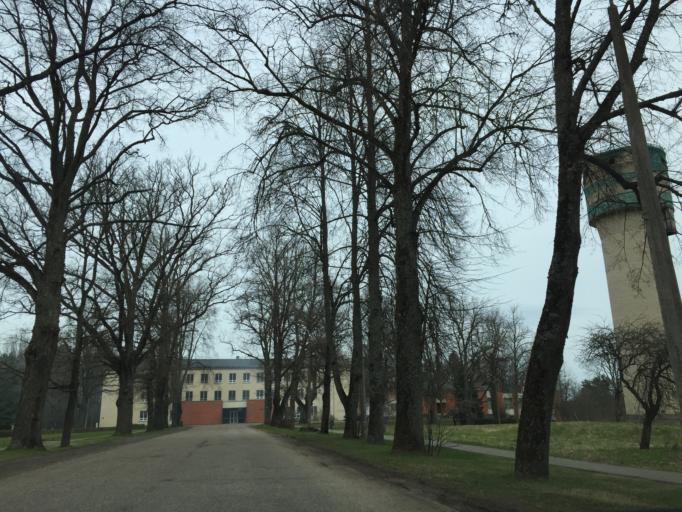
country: LV
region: Priekuli
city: Priekuli
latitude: 57.3533
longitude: 25.3323
